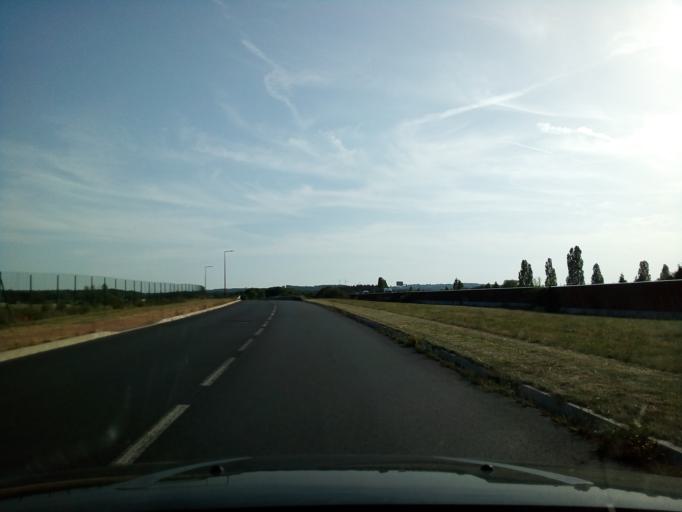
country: FR
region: Auvergne
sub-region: Departement de l'Allier
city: Domerat
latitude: 46.3620
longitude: 2.5539
